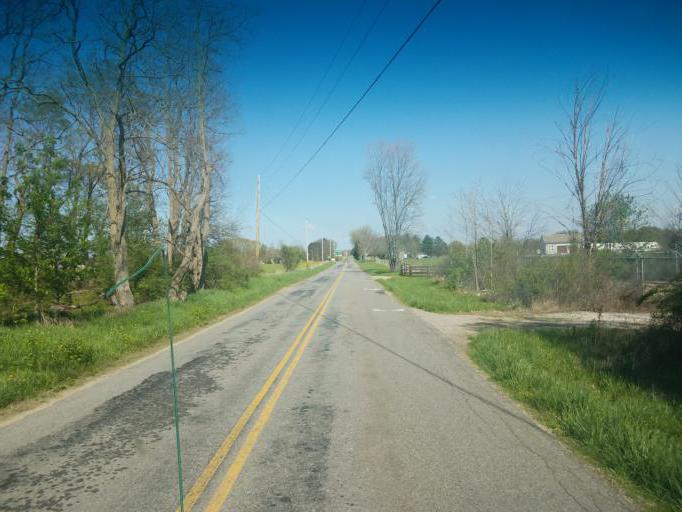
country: US
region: Ohio
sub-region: Medina County
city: Lodi
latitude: 40.9958
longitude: -81.9877
